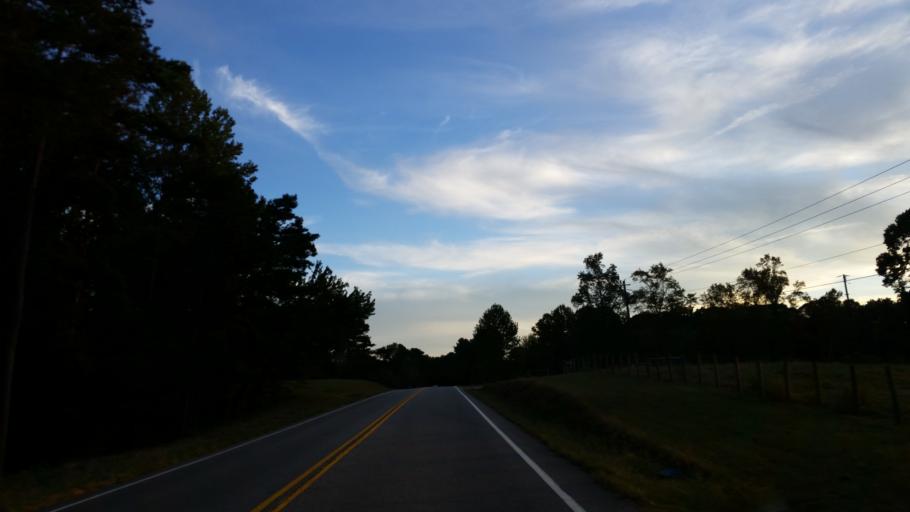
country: US
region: Georgia
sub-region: Dawson County
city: Dawsonville
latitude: 34.3986
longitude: -84.1223
